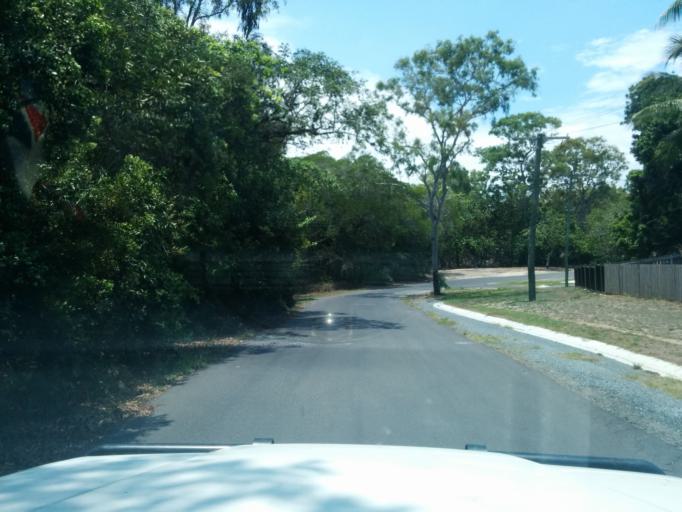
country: AU
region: Queensland
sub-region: Cairns
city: Yorkeys Knob
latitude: -16.8319
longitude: 145.7352
